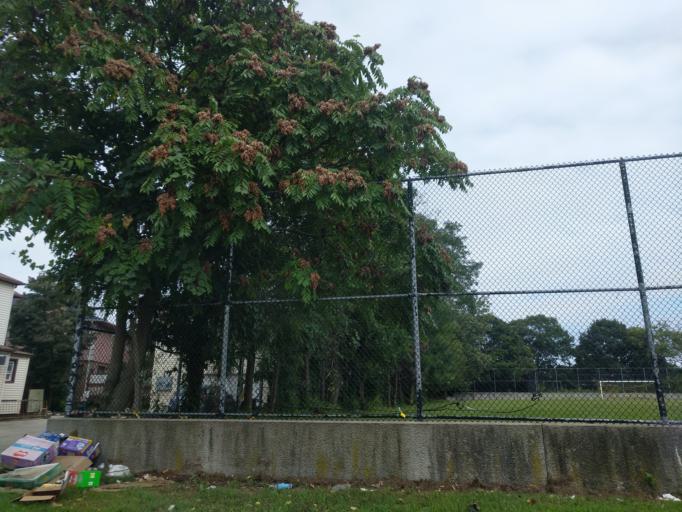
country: US
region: New York
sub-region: Nassau County
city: Lawrence
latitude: 40.6199
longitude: -73.7374
